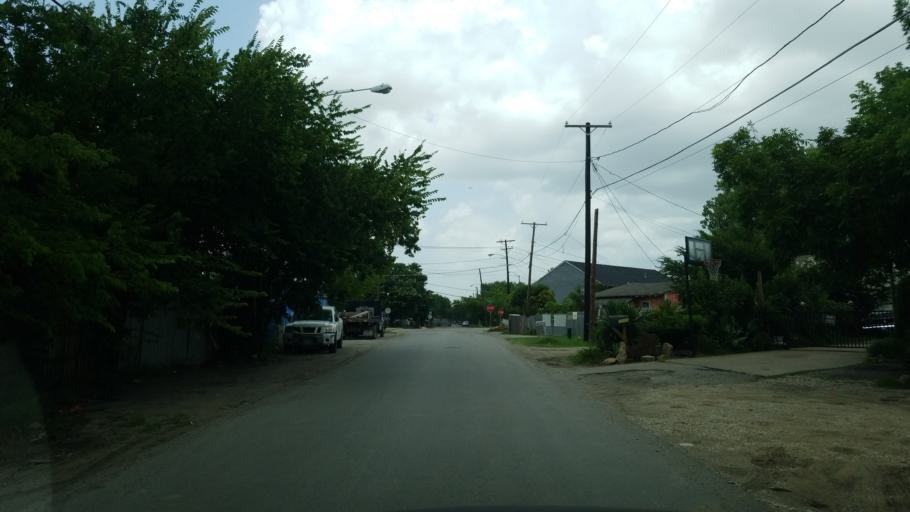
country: US
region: Texas
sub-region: Dallas County
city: Cockrell Hill
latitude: 32.7841
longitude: -96.8989
